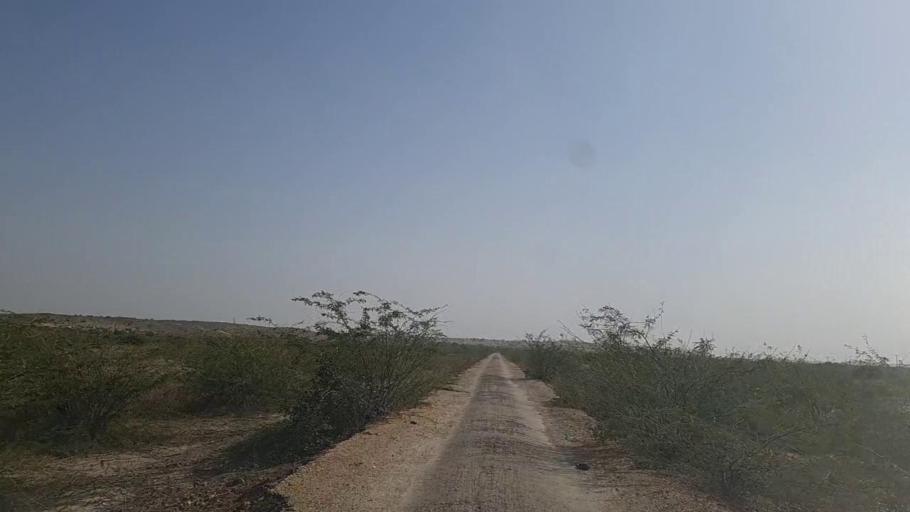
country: PK
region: Sindh
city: Naukot
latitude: 24.5844
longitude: 69.2930
